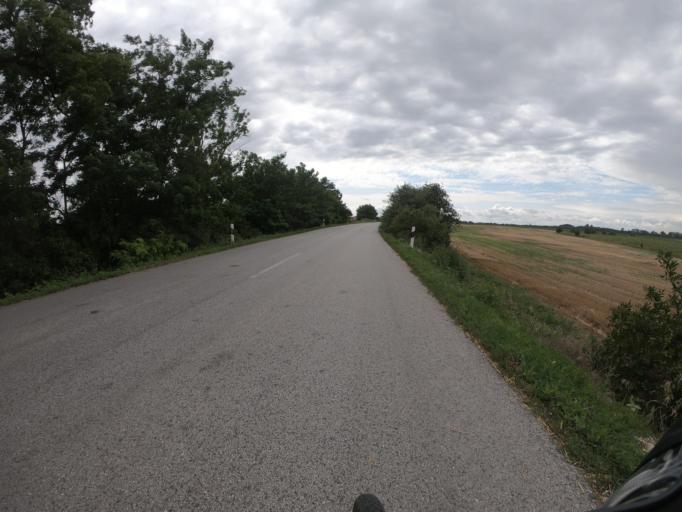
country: HU
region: Heves
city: Poroszlo
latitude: 47.6985
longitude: 20.6953
